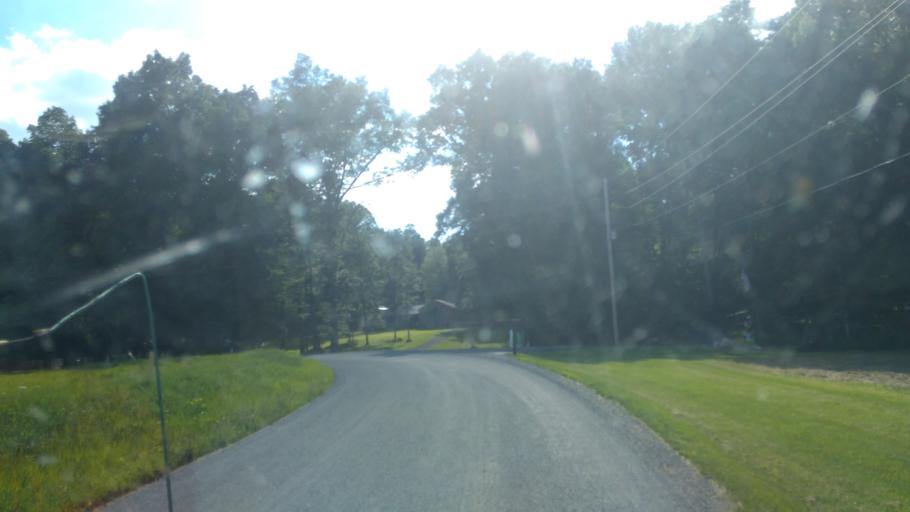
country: US
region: Ohio
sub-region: Wayne County
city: Apple Creek
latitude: 40.7183
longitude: -81.9055
